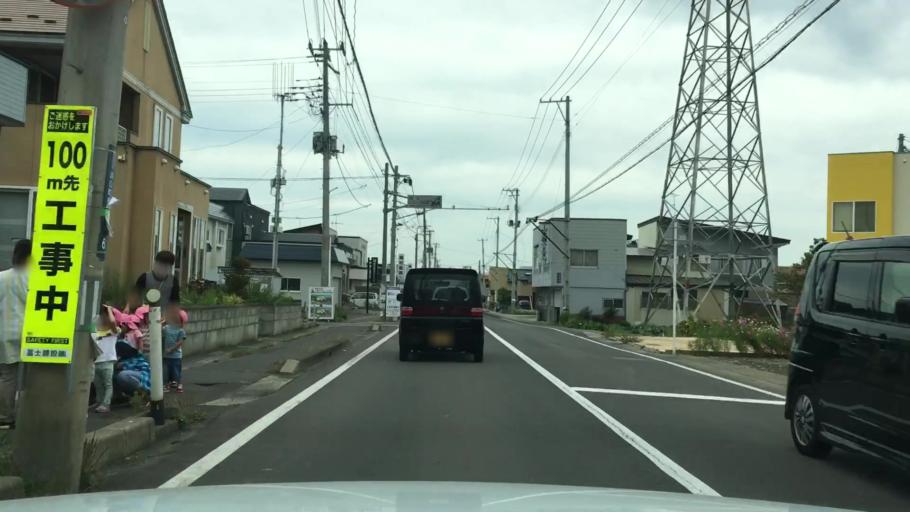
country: JP
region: Aomori
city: Hirosaki
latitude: 40.6259
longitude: 140.4555
